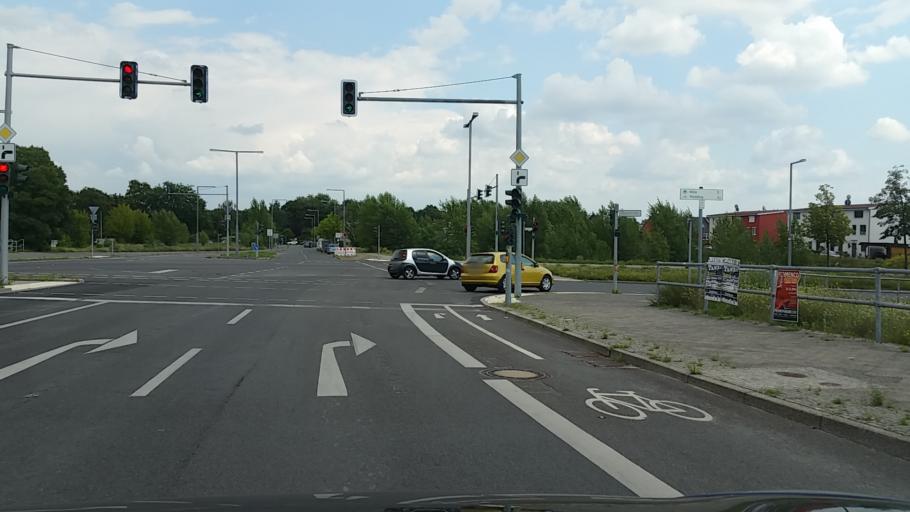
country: DE
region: Berlin
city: Haselhorst
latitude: 52.5590
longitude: 13.2272
